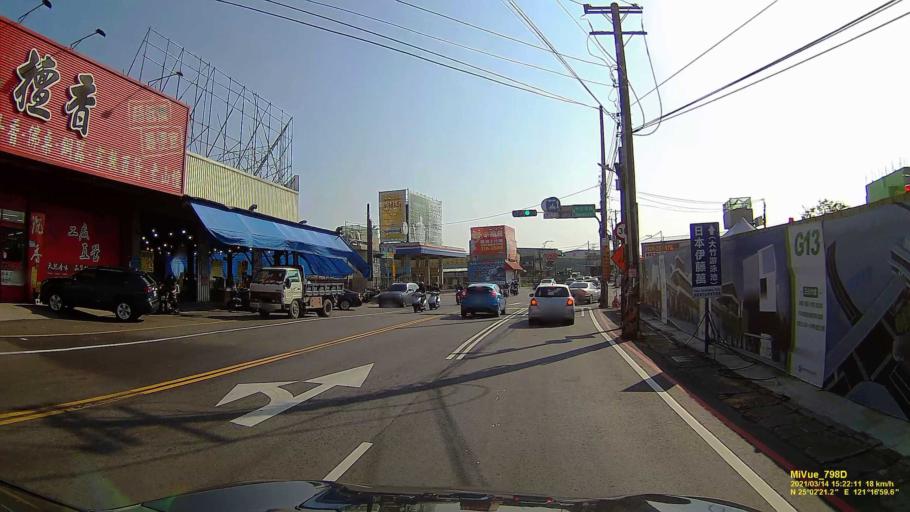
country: TW
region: Taiwan
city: Taoyuan City
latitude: 25.0391
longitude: 121.2831
